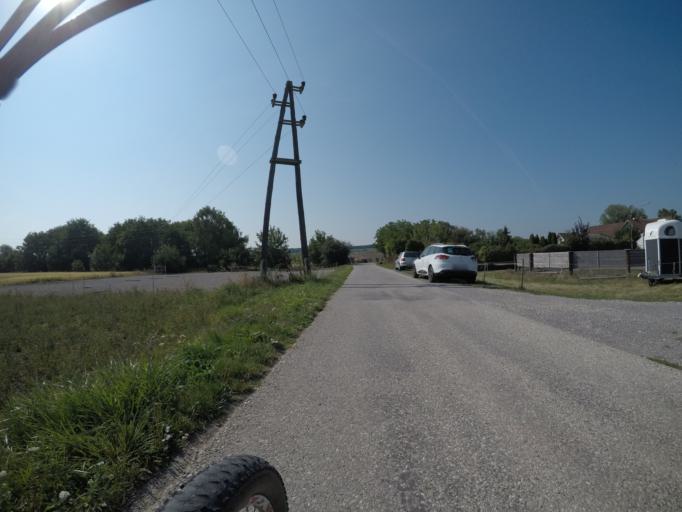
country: AT
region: Lower Austria
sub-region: Politischer Bezirk Baden
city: Bad Voslau
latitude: 47.9574
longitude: 16.1887
